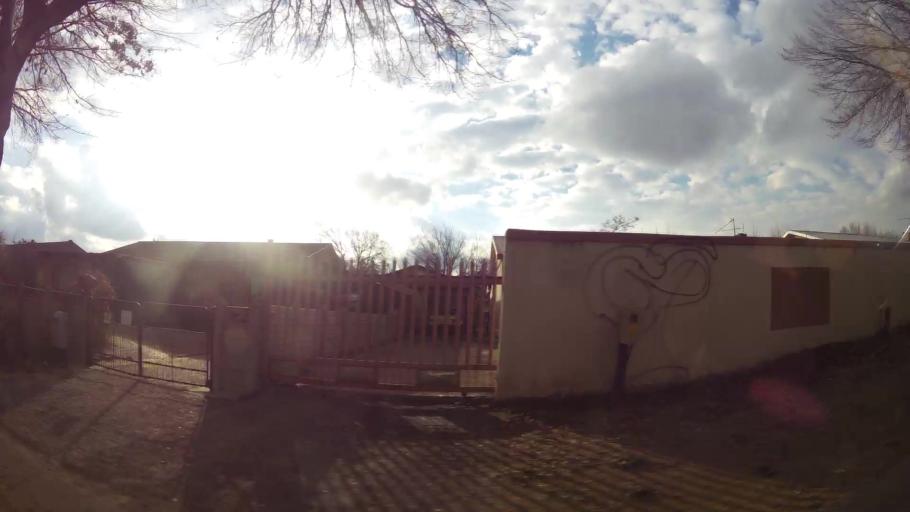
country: ZA
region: Orange Free State
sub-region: Fezile Dabi District Municipality
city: Sasolburg
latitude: -26.8255
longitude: 27.8280
